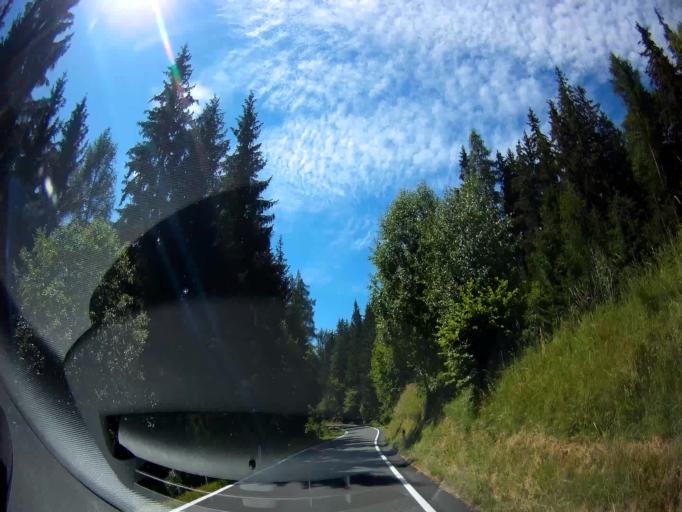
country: AT
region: Carinthia
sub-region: Politischer Bezirk Sankt Veit an der Glan
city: Glodnitz
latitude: 46.9165
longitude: 14.0694
